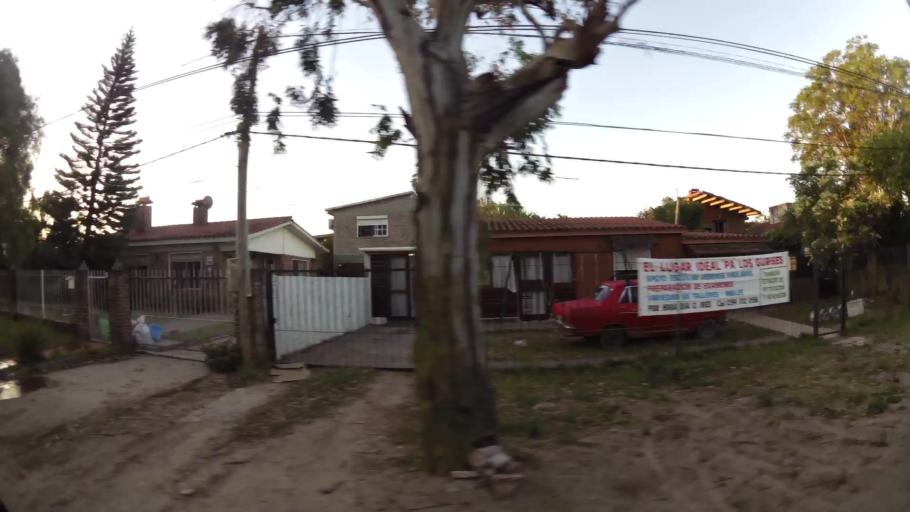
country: UY
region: Canelones
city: Barra de Carrasco
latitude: -34.8418
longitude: -55.9895
